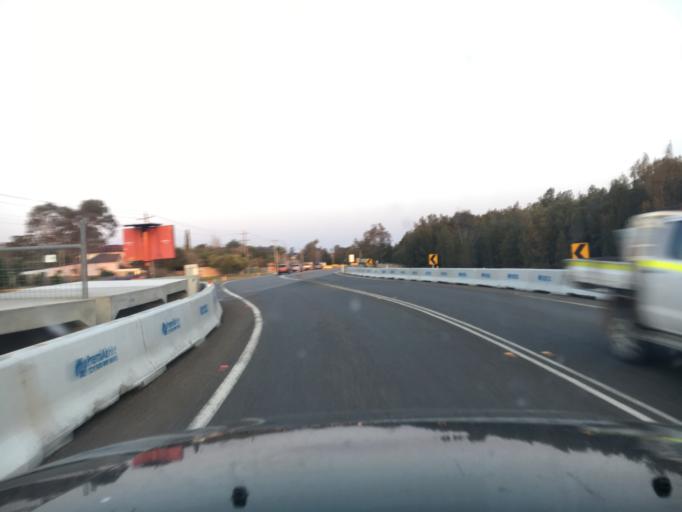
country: AU
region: New South Wales
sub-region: Cessnock
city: Greta
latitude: -32.6728
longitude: 151.3815
